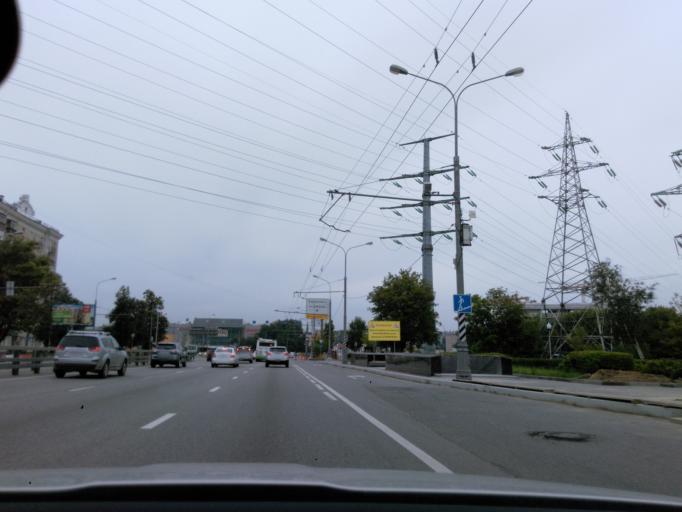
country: RU
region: Moscow
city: Nagornyy
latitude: 55.6618
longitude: 37.6344
